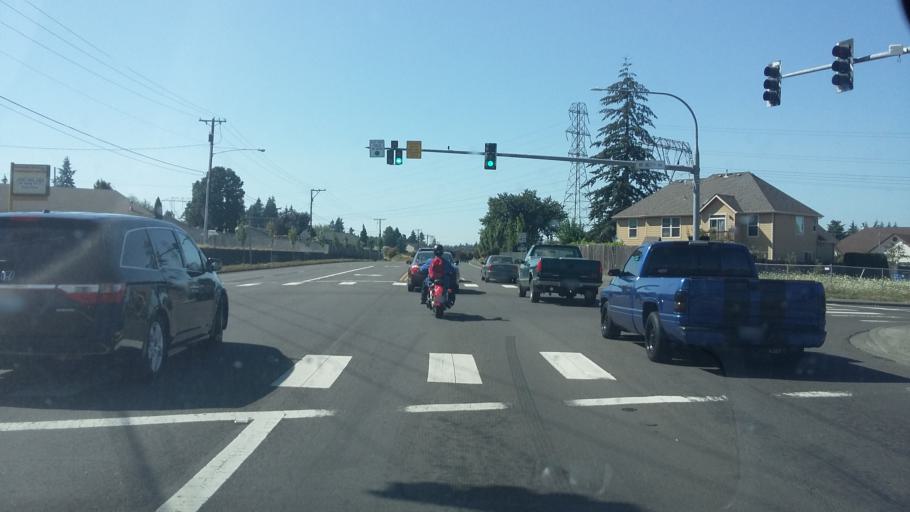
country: US
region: Washington
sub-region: Clark County
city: Orchards
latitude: 45.6685
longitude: -122.5636
